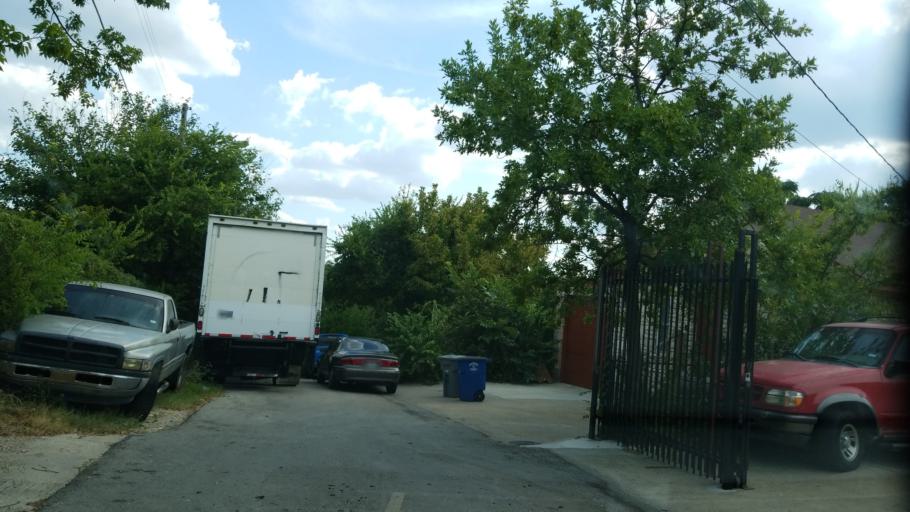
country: US
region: Texas
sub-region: Dallas County
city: Dallas
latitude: 32.7647
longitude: -96.8453
